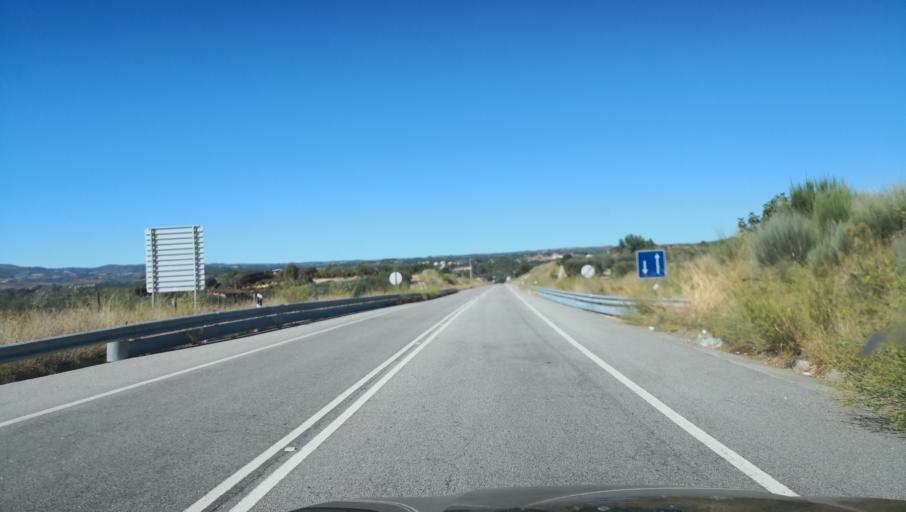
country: PT
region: Vila Real
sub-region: Valpacos
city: Valpacos
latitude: 41.5743
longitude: -7.3009
